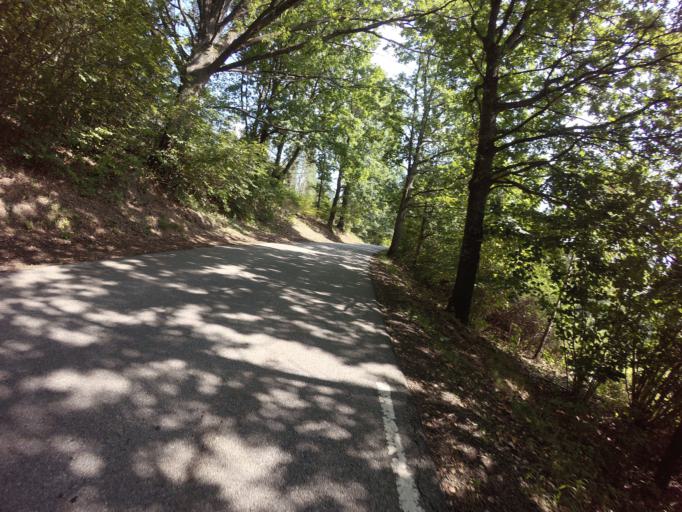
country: CZ
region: Jihocesky
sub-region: Okres Cesky Krumlov
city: Vyssi Brod
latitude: 48.6455
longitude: 14.3583
